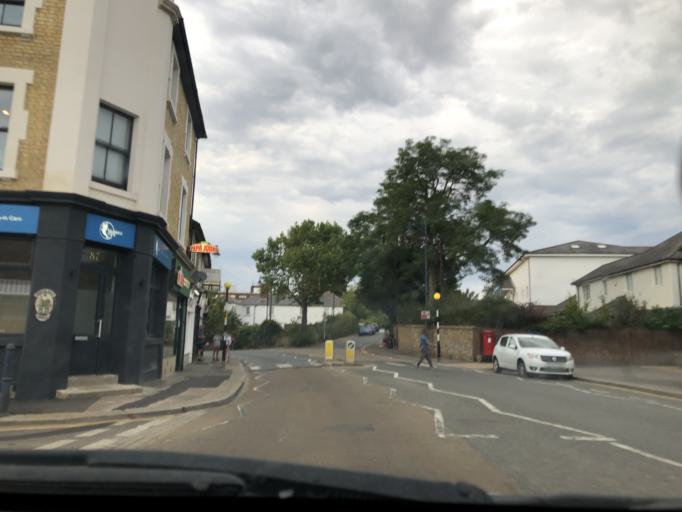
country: GB
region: England
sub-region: Kent
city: Sevenoaks
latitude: 51.2866
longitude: 0.1957
